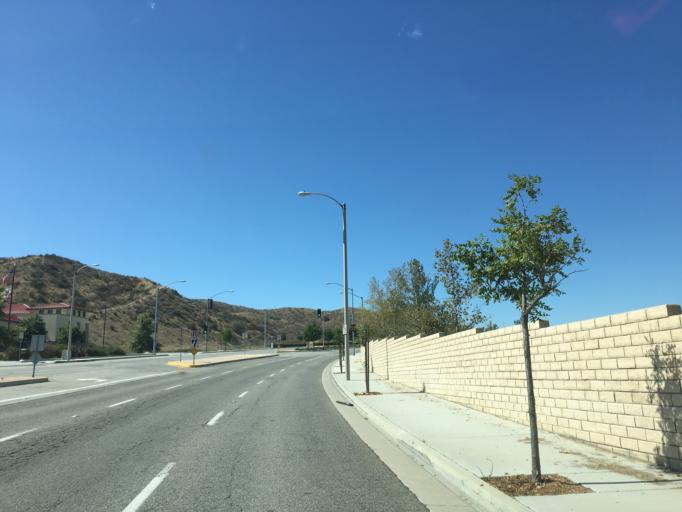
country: US
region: California
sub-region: Los Angeles County
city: Santa Clarita
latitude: 34.4430
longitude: -118.4729
